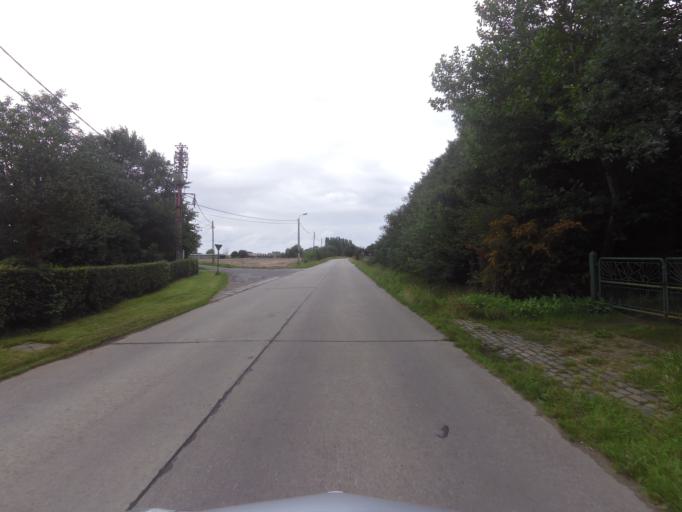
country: BE
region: Flanders
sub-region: Provincie West-Vlaanderen
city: Lichtervelde
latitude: 51.0510
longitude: 3.1937
